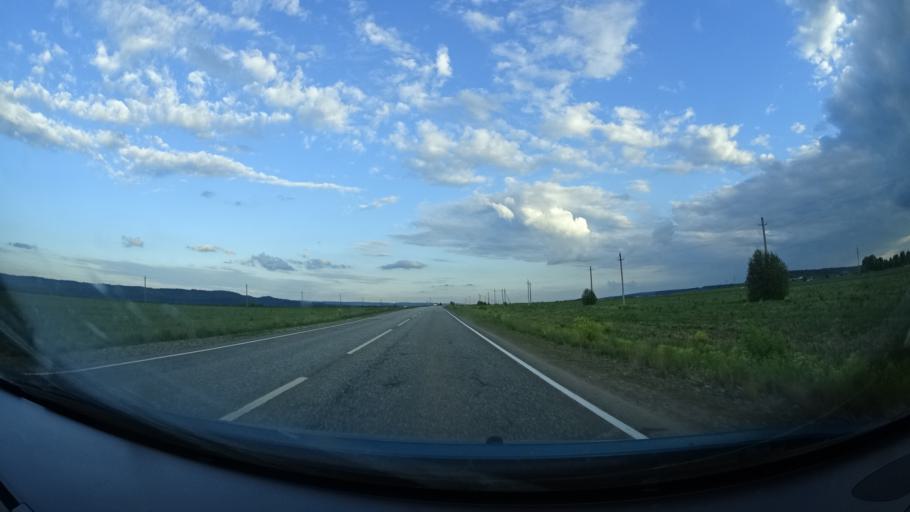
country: RU
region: Perm
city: Barda
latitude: 56.9923
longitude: 55.5724
